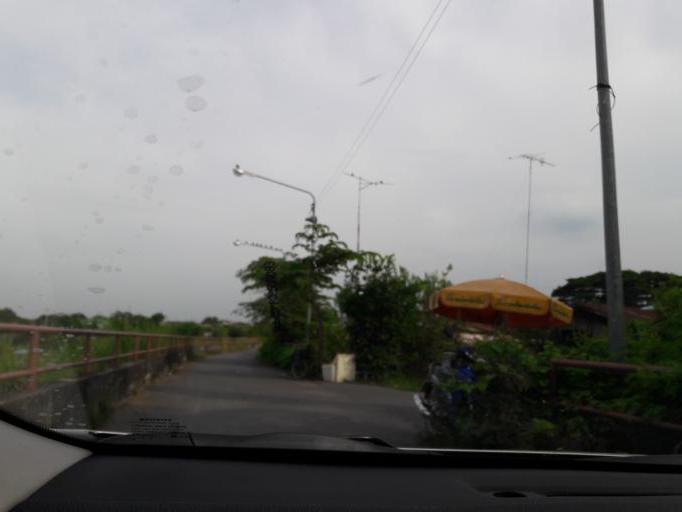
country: TH
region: Ang Thong
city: Ang Thong
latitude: 14.5883
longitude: 100.4589
